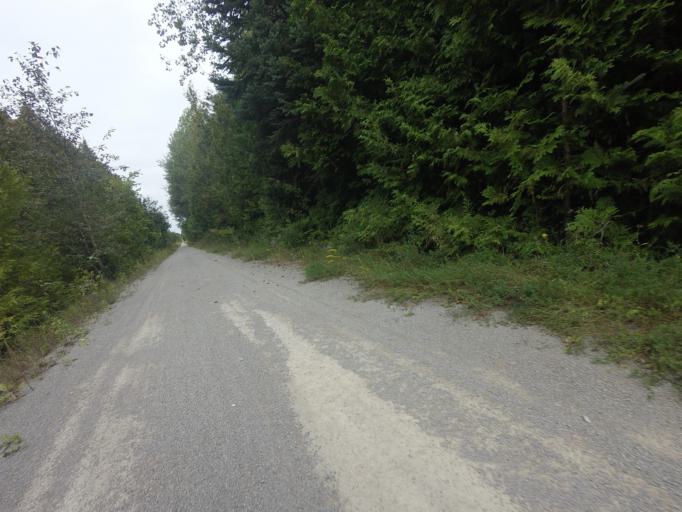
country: CA
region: Ontario
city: Uxbridge
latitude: 44.2754
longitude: -79.0125
